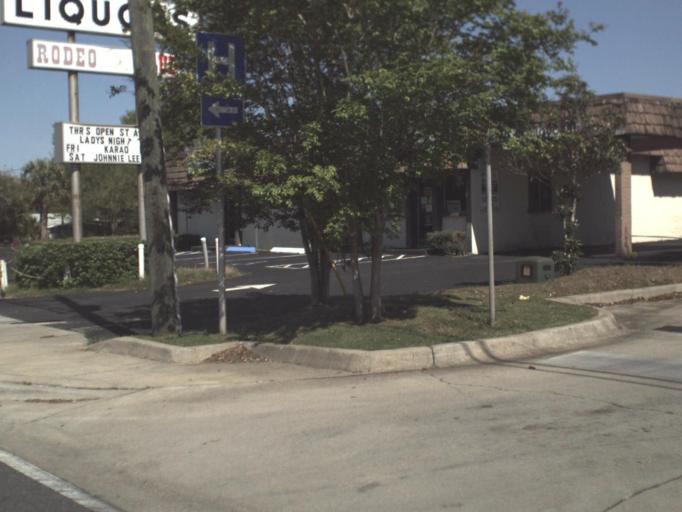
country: US
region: Florida
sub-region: Okaloosa County
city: Wright
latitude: 30.4273
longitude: -86.6397
